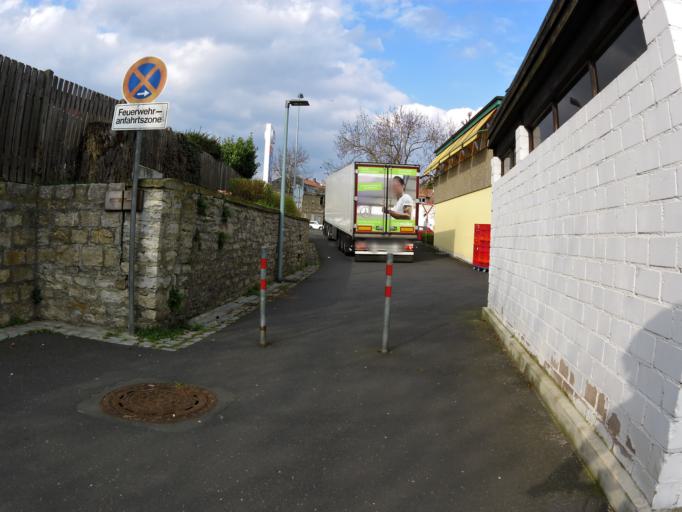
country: DE
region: Bavaria
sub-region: Regierungsbezirk Unterfranken
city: Kitzingen
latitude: 49.7385
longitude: 10.1517
